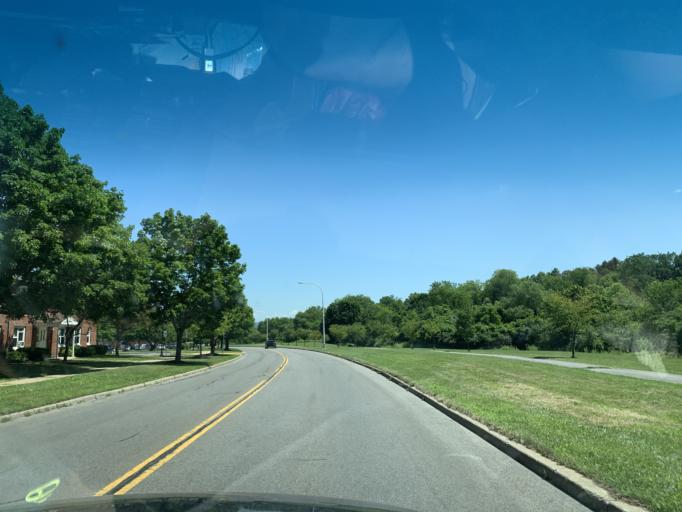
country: US
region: New York
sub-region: Oneida County
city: Utica
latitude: 43.0766
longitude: -75.2104
